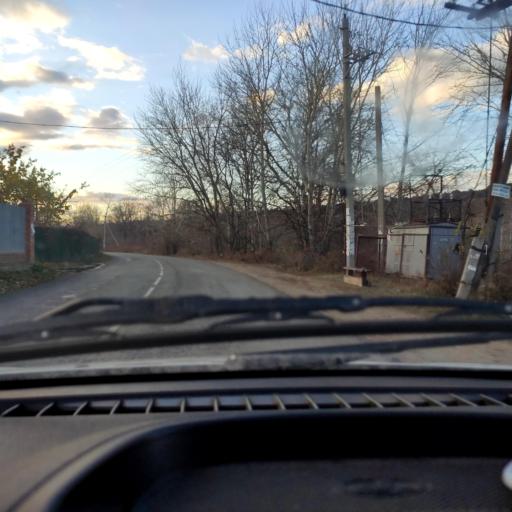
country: RU
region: Samara
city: Povolzhskiy
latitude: 53.4655
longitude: 49.6670
